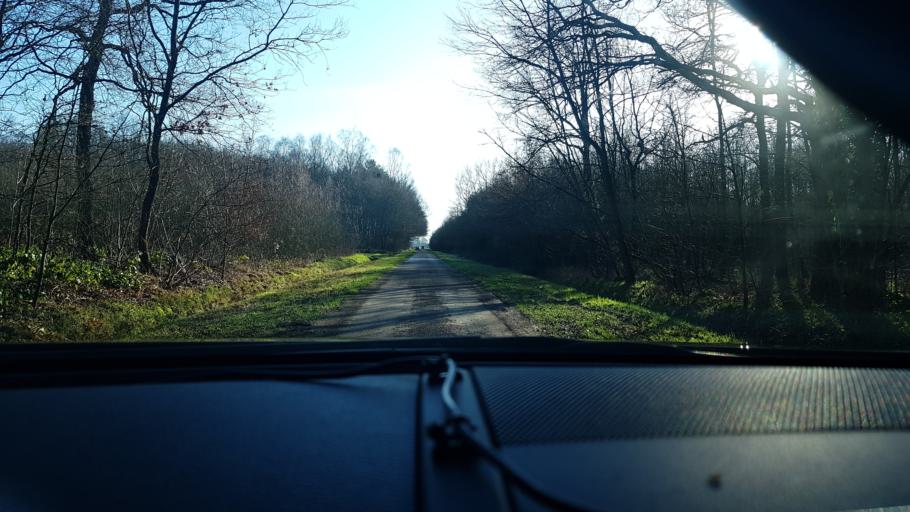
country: NL
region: Limburg
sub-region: Gemeente Leudal
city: Haelen
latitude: 51.2822
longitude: 5.9838
